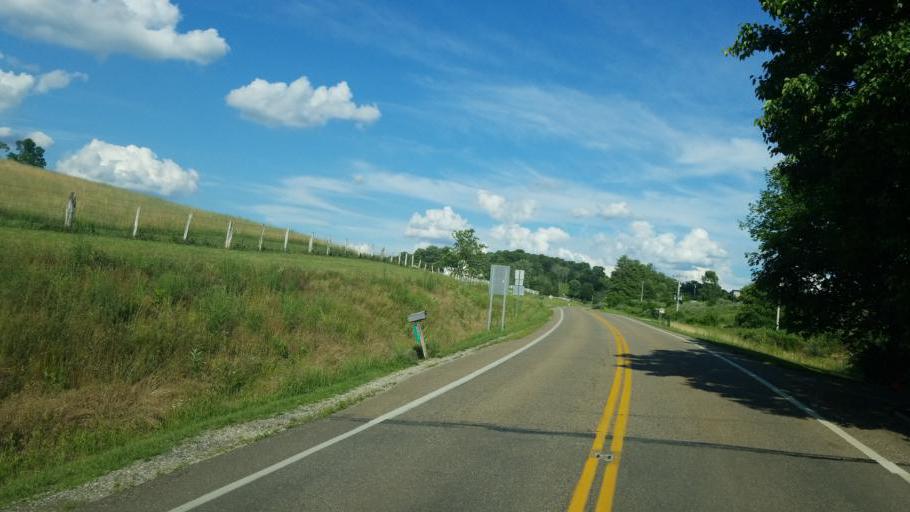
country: US
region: Ohio
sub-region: Gallia County
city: Gallipolis
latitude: 38.8065
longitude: -82.3140
